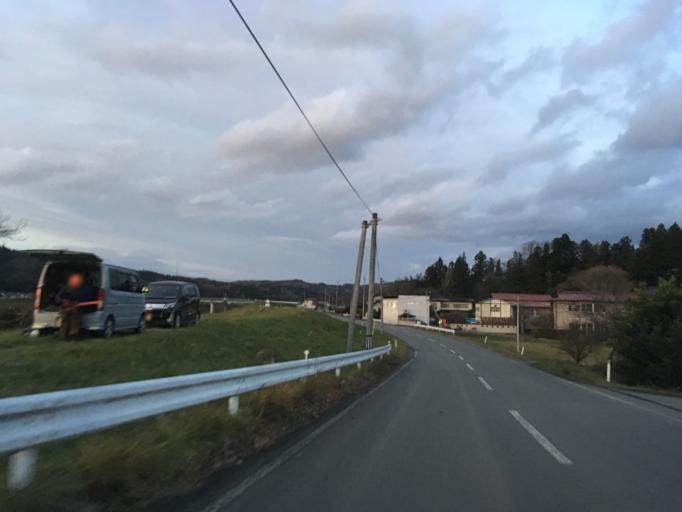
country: JP
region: Iwate
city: Ichinoseki
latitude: 38.8340
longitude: 141.2667
